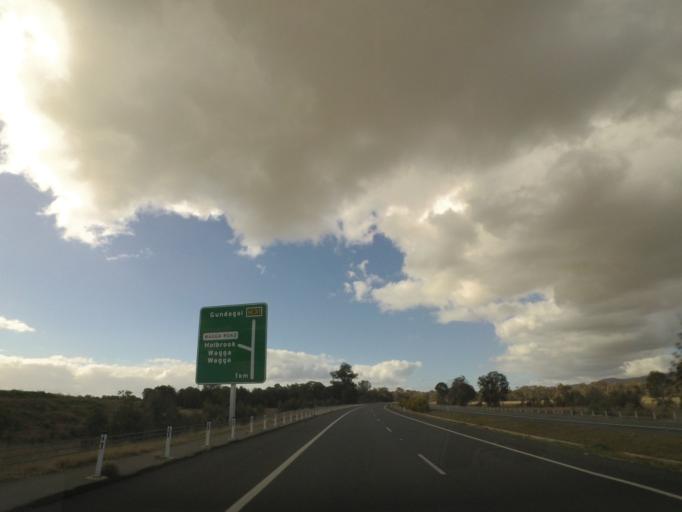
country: AU
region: New South Wales
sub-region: Greater Hume Shire
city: Holbrook
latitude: -35.7094
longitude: 147.3068
